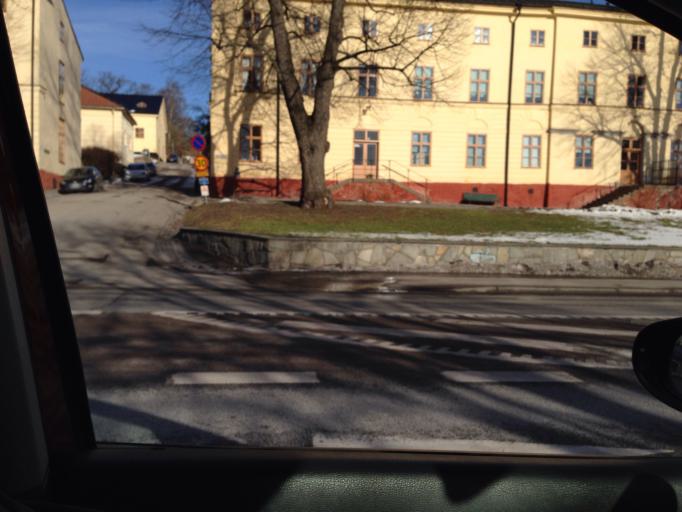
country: SE
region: Stockholm
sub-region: Stockholms Kommun
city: Bromma
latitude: 59.3241
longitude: 17.8883
